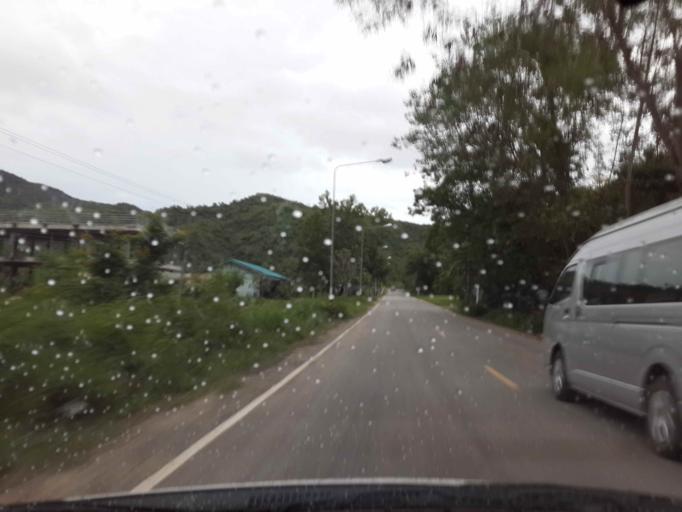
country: TH
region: Ratchaburi
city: Suan Phueng
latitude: 13.5864
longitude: 99.2473
